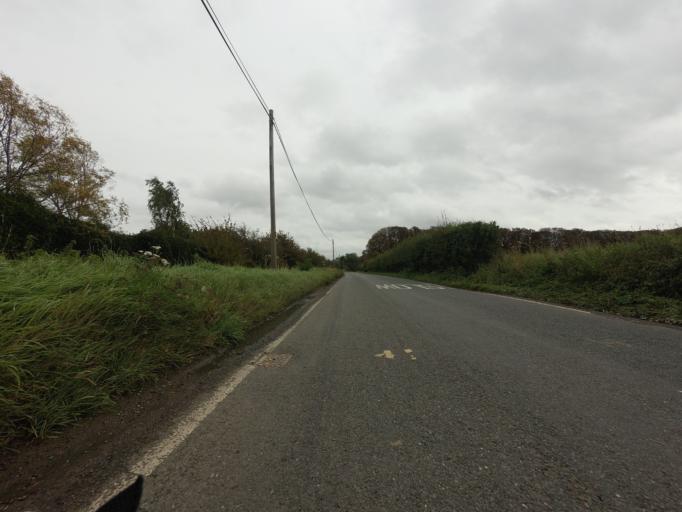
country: GB
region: England
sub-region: Cambridgeshire
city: Duxford
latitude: 52.0200
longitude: 0.1272
